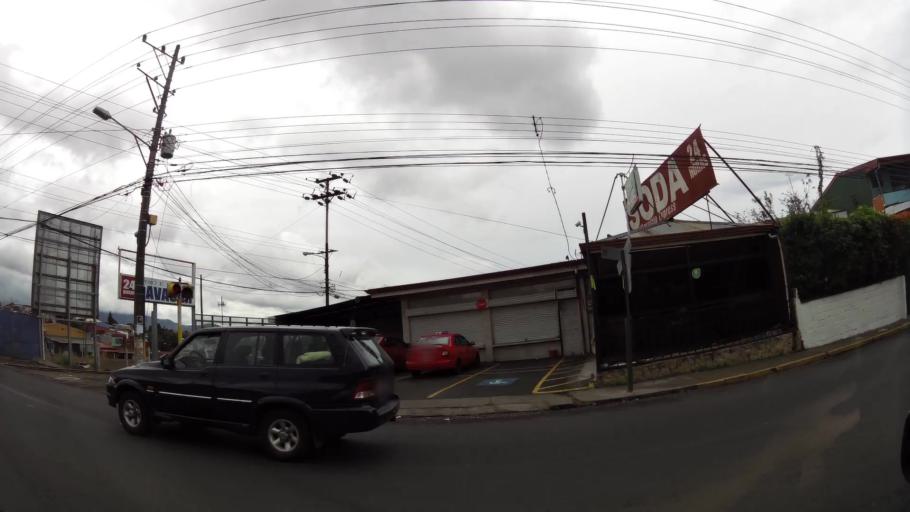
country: CR
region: San Jose
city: Colima
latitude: 9.9496
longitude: -84.0787
